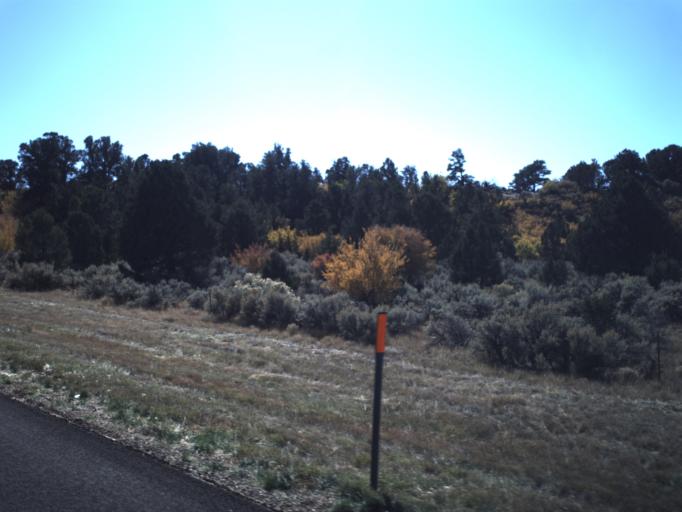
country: US
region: Utah
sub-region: Garfield County
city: Panguitch
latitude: 37.6422
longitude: -111.8448
